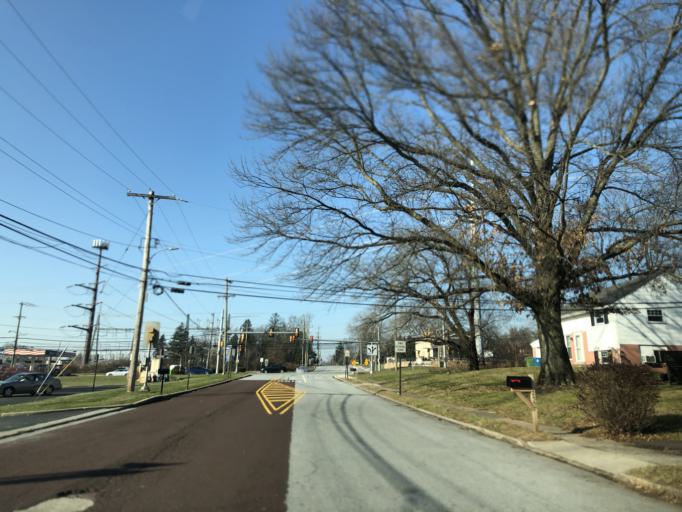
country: US
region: Pennsylvania
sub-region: Montgomery County
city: Audubon
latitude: 40.1138
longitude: -75.4175
